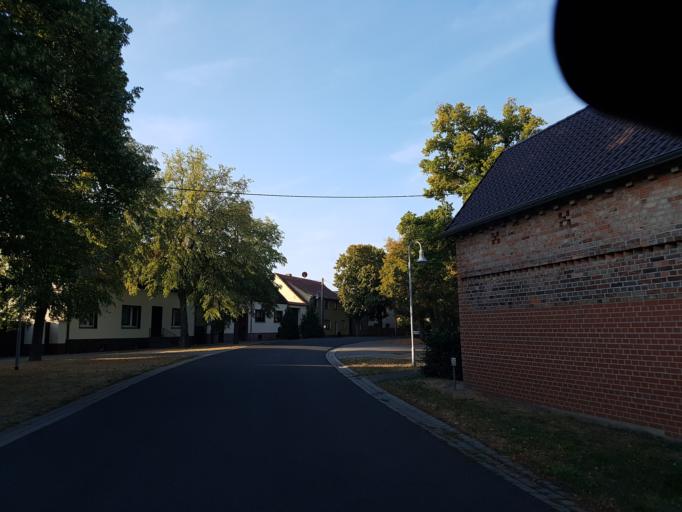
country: DE
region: Saxony-Anhalt
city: Holzdorf
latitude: 51.8324
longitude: 13.1255
